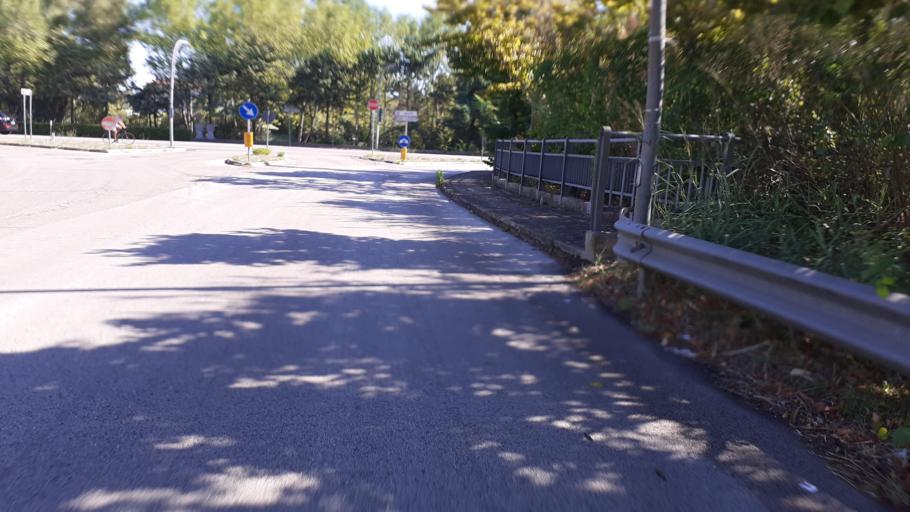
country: IT
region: Abruzzo
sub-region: Provincia di Chieti
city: Marina di Vasto
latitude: 42.0819
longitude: 14.7420
